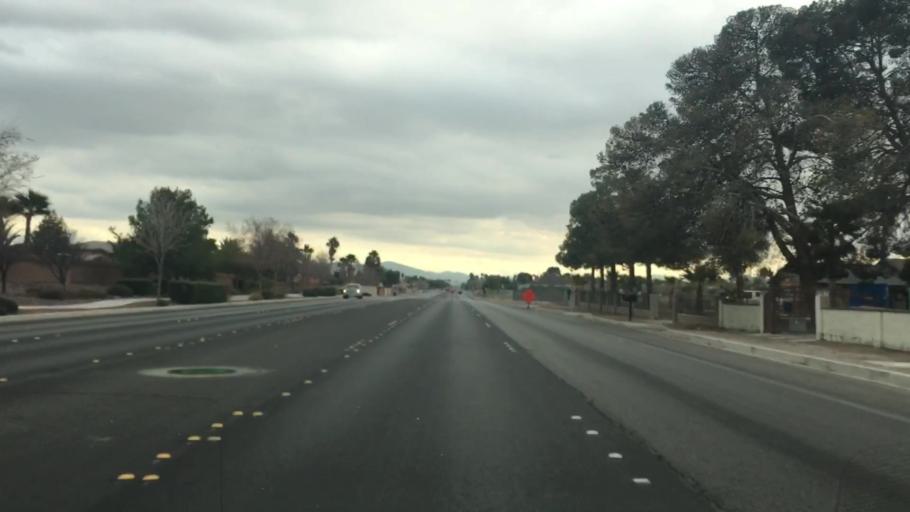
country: US
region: Nevada
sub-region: Clark County
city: Paradise
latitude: 36.0476
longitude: -115.1545
